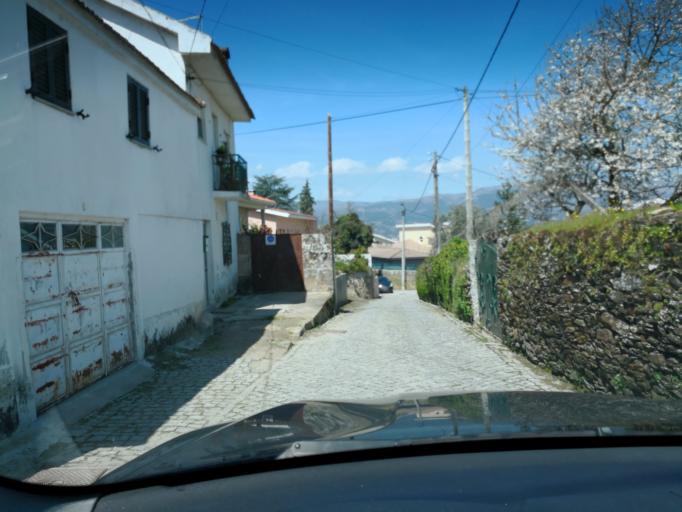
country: PT
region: Vila Real
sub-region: Vila Real
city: Vila Real
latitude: 41.2812
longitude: -7.7299
